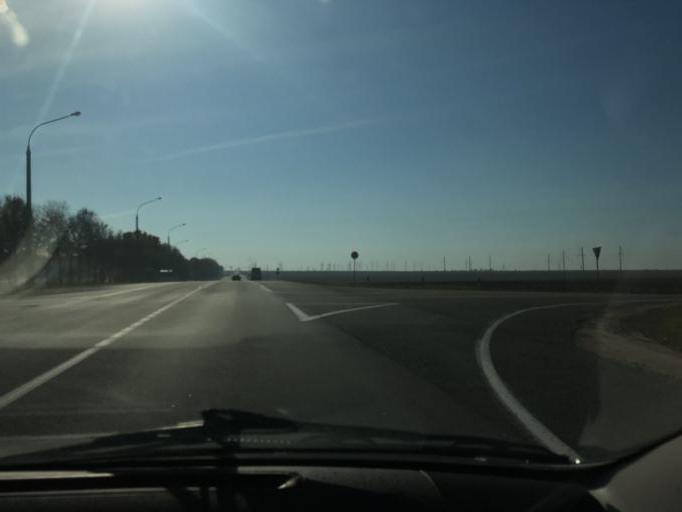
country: BY
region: Minsk
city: Salihorsk
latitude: 52.8740
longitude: 27.4672
